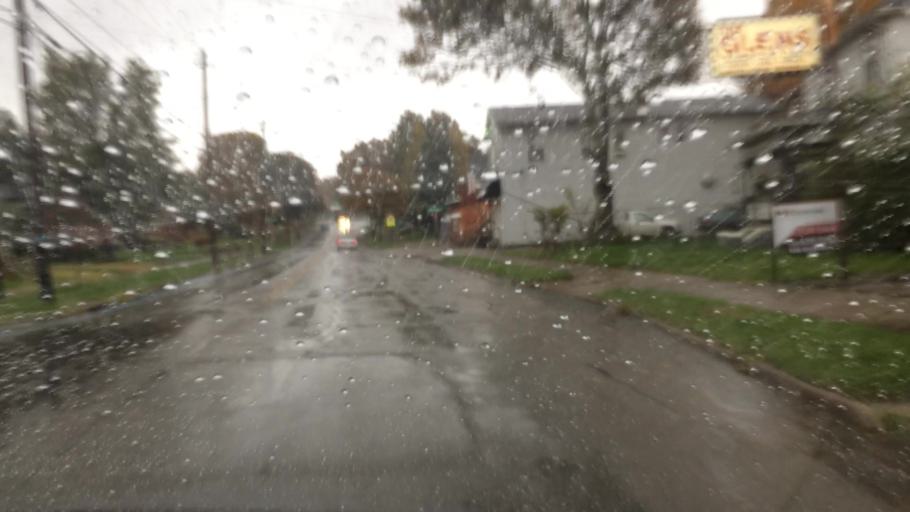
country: US
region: Ohio
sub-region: Summit County
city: Akron
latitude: 41.0970
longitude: -81.5033
